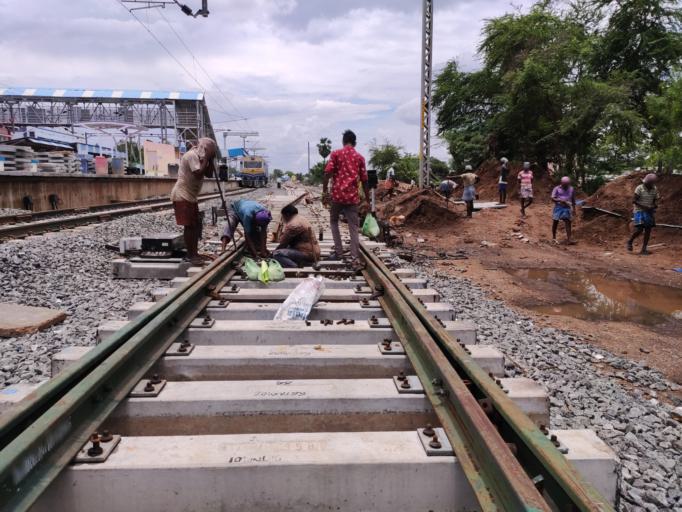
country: IN
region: Tamil Nadu
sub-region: Thoothukkudi
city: Kovilpatti
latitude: 9.1832
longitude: 77.8734
